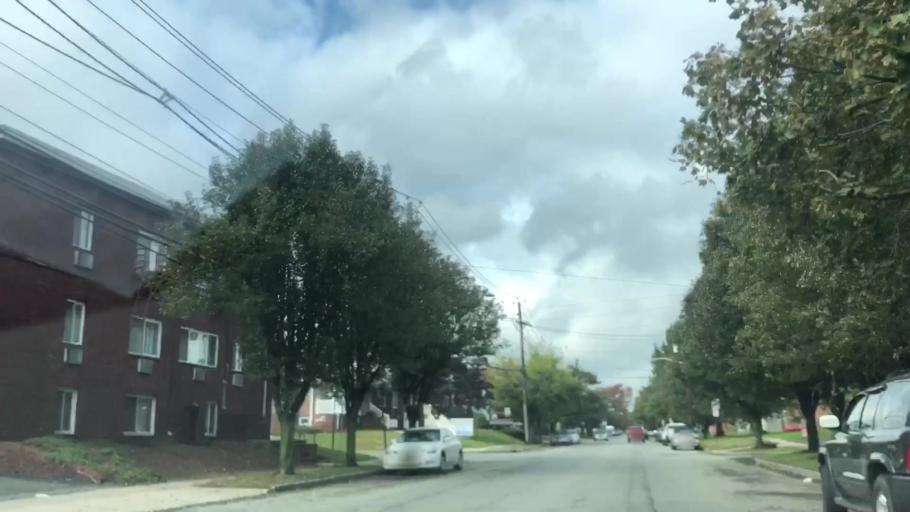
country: US
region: New Jersey
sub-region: Essex County
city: Bloomfield
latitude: 40.7844
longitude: -74.1785
